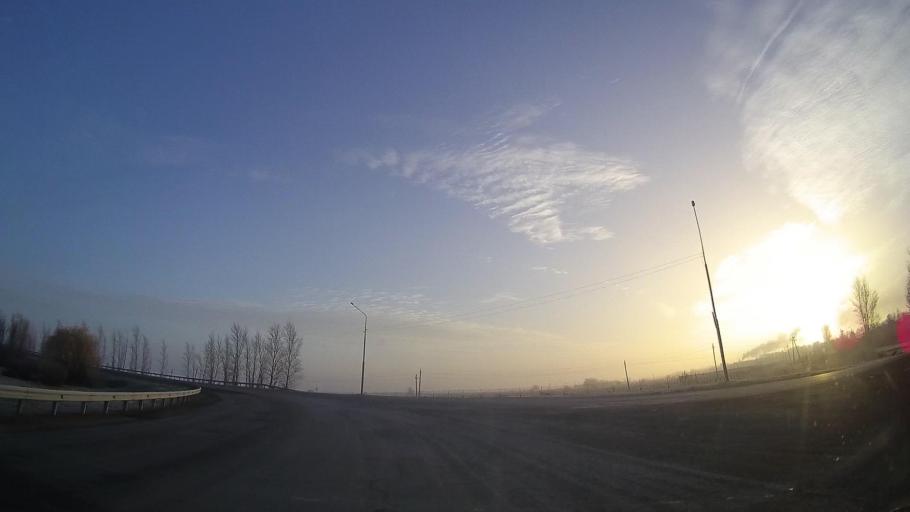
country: RU
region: Rostov
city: Bataysk
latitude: 47.1014
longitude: 39.7655
